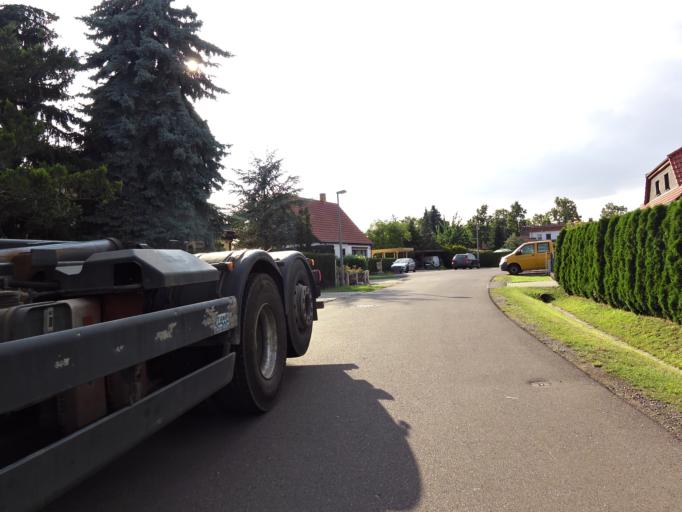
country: DE
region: Saxony
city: Zwenkau
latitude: 51.2694
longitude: 12.3047
